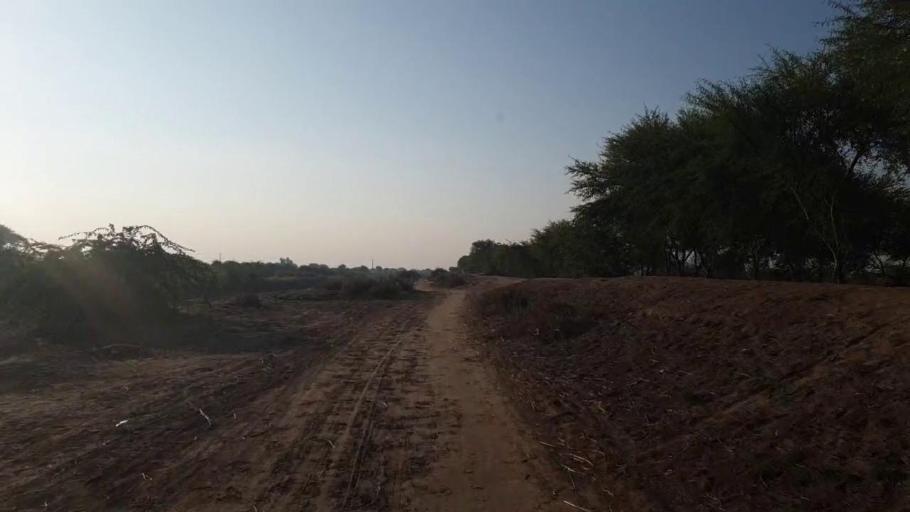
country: PK
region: Sindh
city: Badin
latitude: 24.6347
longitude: 68.7943
